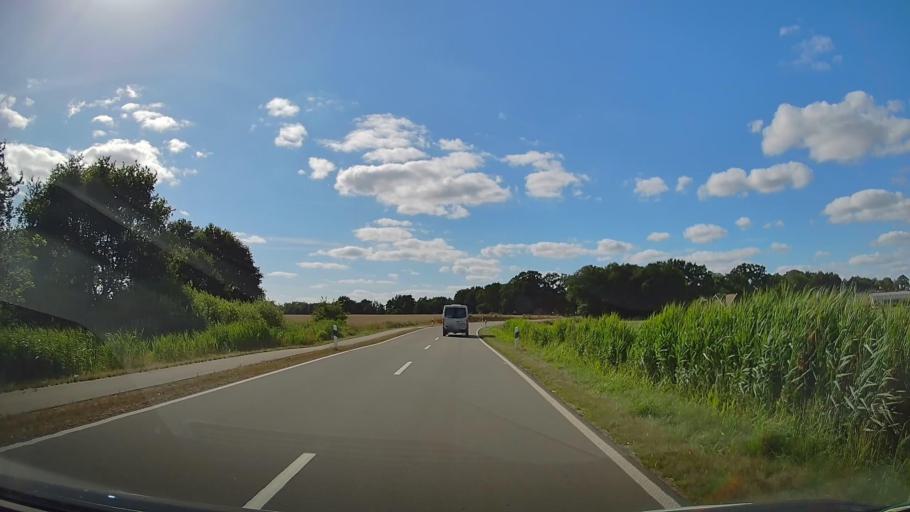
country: DE
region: Lower Saxony
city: Loningen
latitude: 52.6914
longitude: 7.7674
